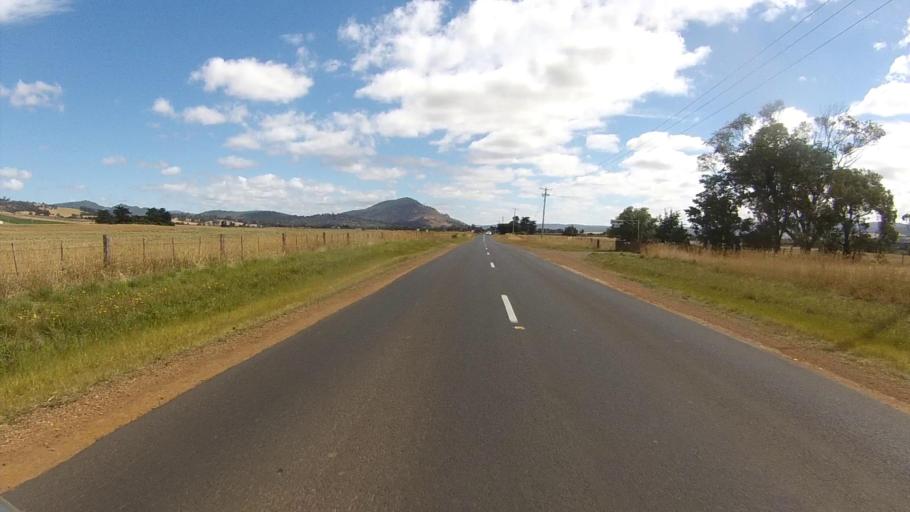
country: AU
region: Tasmania
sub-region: Clarence
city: Cambridge
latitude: -42.7046
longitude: 147.4299
